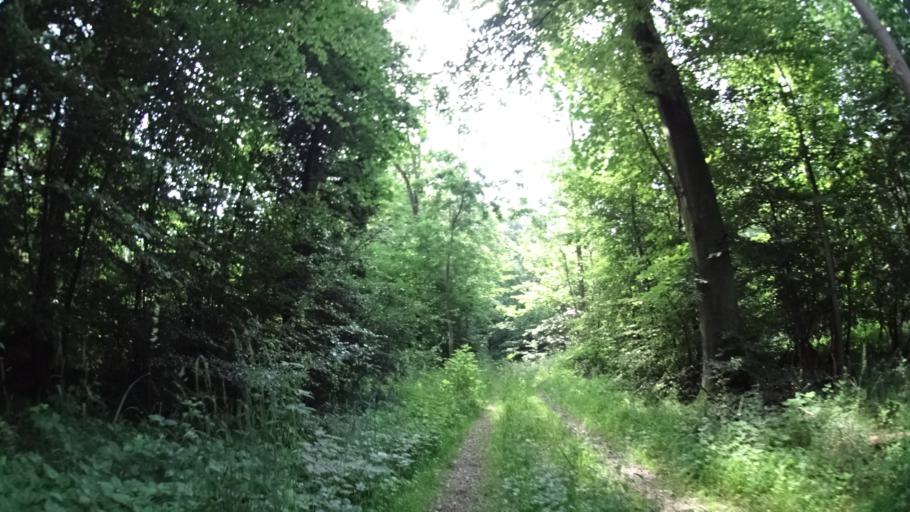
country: DK
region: Central Jutland
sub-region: Arhus Kommune
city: Stavtrup
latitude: 56.1401
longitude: 10.1005
